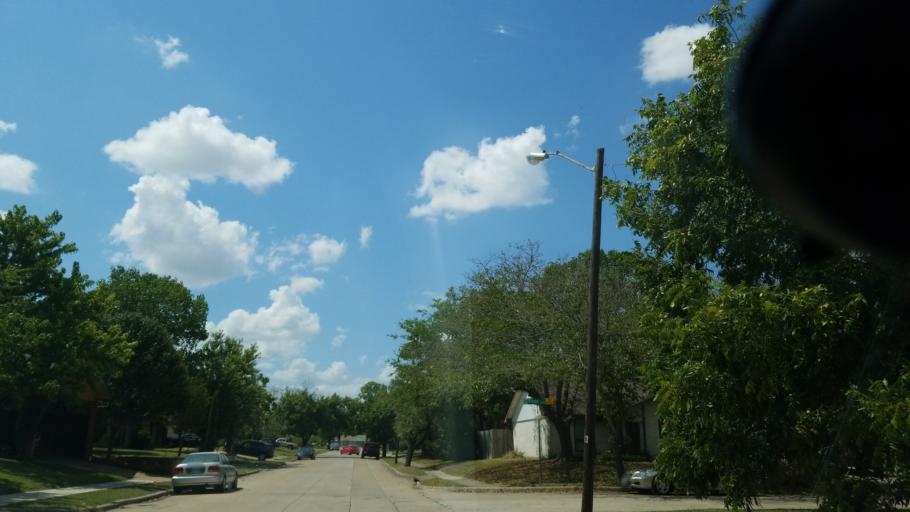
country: US
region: Texas
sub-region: Dallas County
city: Grand Prairie
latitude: 32.7225
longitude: -96.9974
